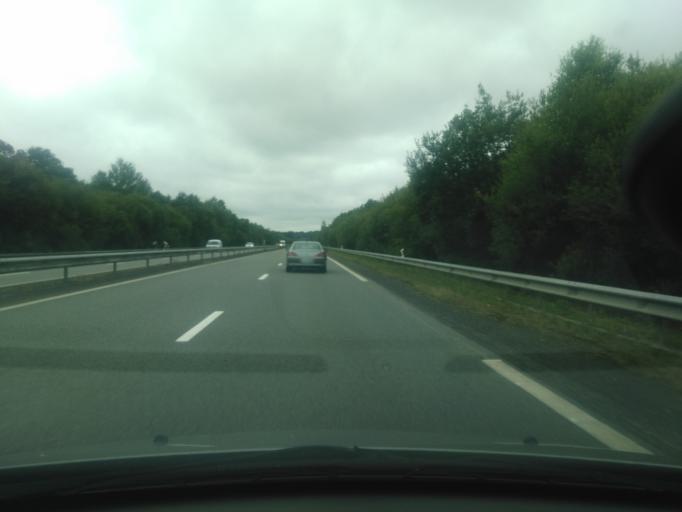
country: FR
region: Brittany
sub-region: Departement des Cotes-d'Armor
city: Plelan-le-Petit
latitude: 48.4253
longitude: -2.1969
